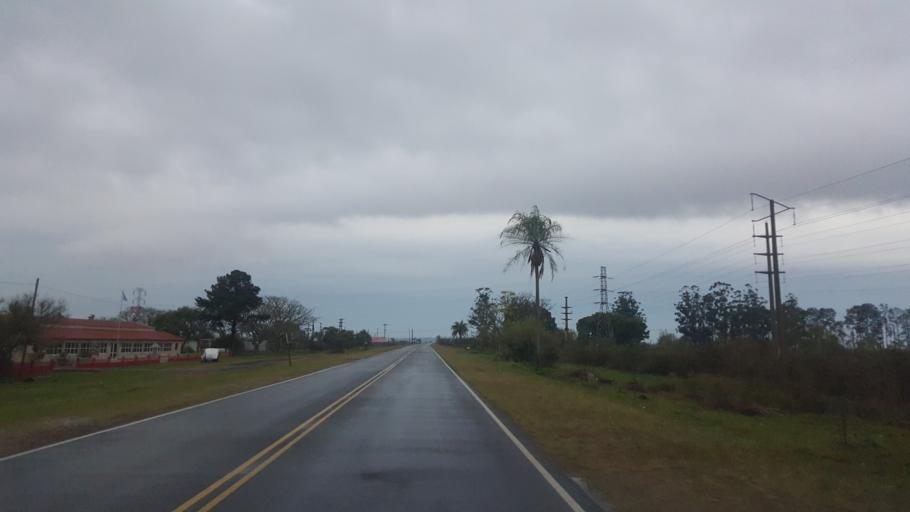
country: AR
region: Corrientes
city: Ituzaingo
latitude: -27.5667
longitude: -56.6629
